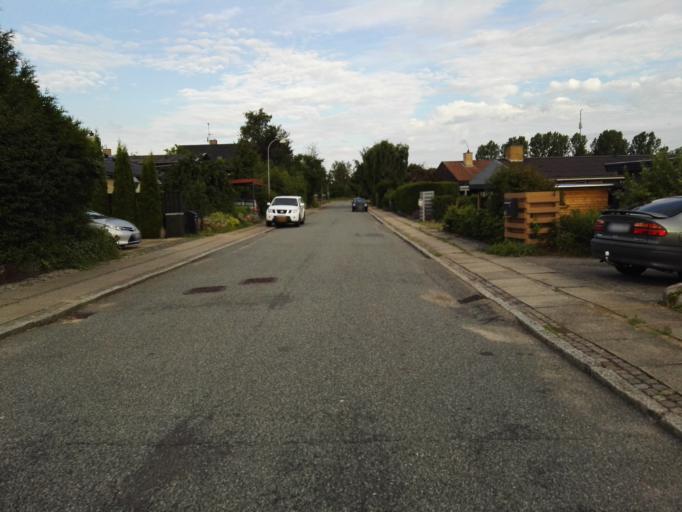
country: DK
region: Capital Region
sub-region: Ballerup Kommune
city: Malov
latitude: 55.7587
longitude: 12.3232
